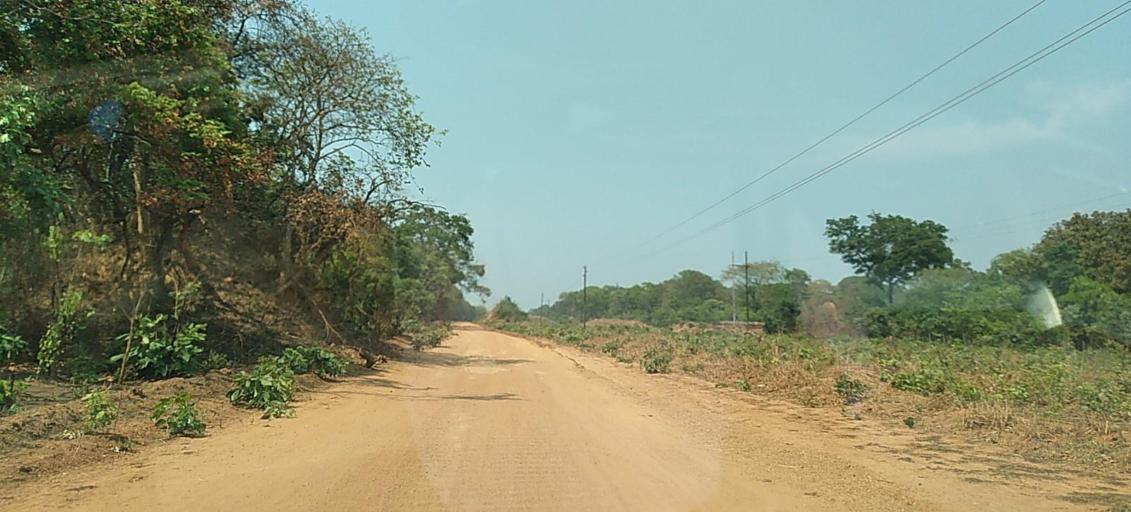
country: ZM
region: Copperbelt
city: Chingola
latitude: -13.0503
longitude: 27.4296
